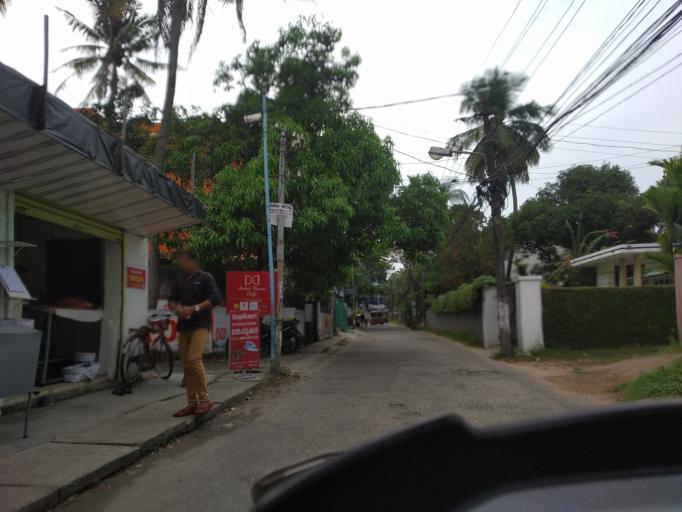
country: IN
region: Kerala
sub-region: Ernakulam
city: Cochin
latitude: 9.9484
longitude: 76.2945
